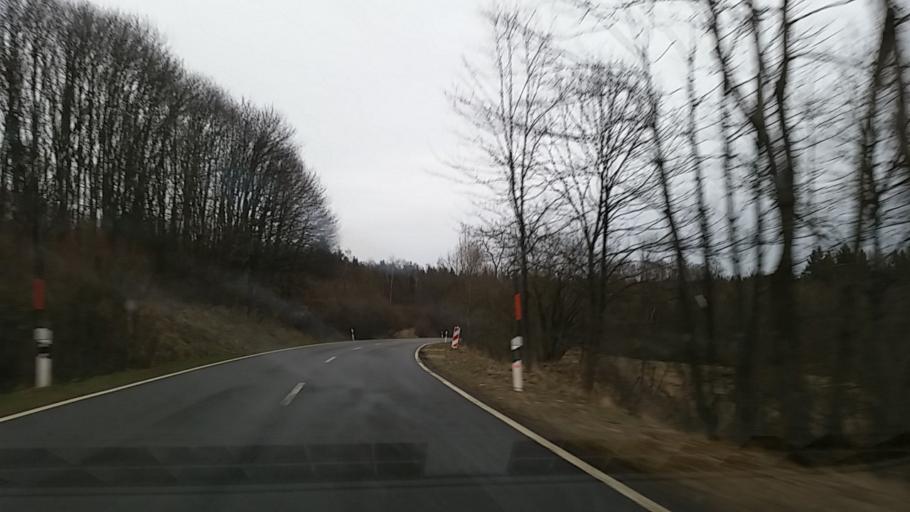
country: DE
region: Saxony-Anhalt
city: Benneckenstein
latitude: 51.6608
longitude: 10.6785
